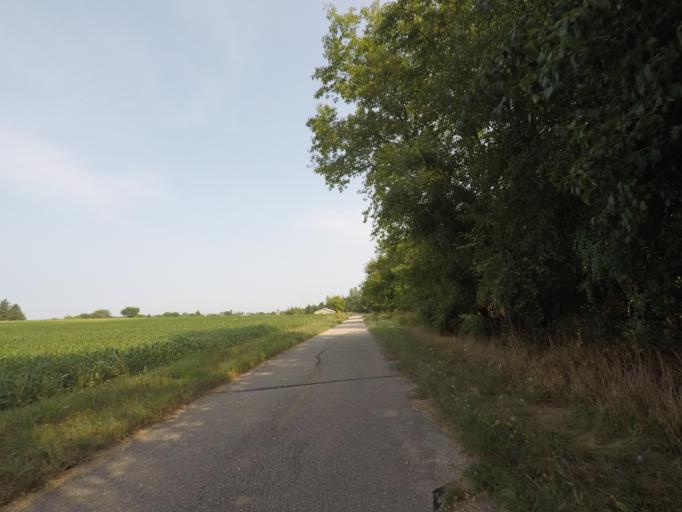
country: US
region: Wisconsin
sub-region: Waukesha County
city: Dousman
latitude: 43.0164
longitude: -88.4471
